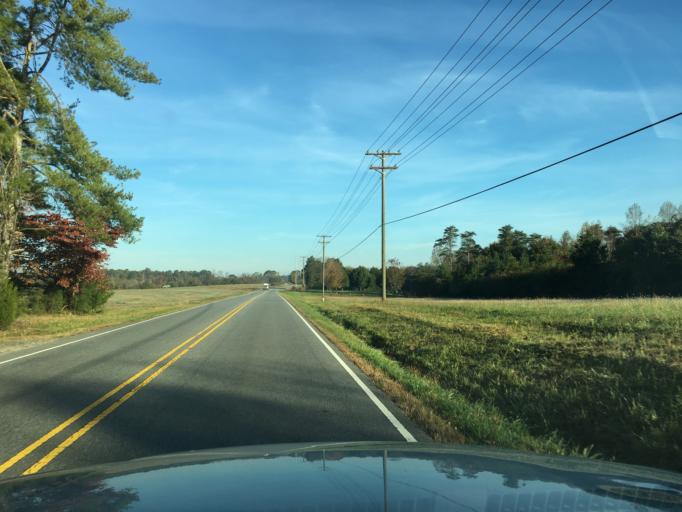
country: US
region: North Carolina
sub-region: Catawba County
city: Maiden
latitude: 35.6128
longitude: -81.2567
